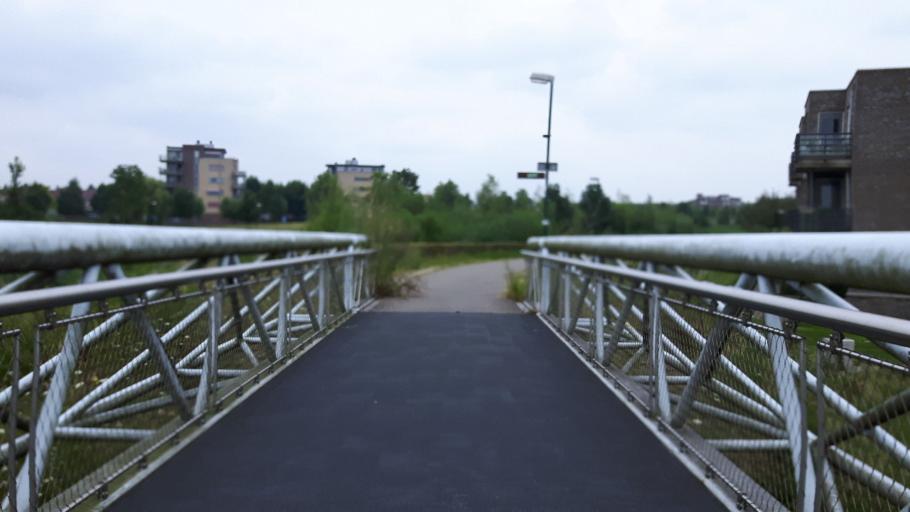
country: NL
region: Utrecht
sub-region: Gemeente Houten
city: Houten
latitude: 52.0114
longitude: 5.1668
